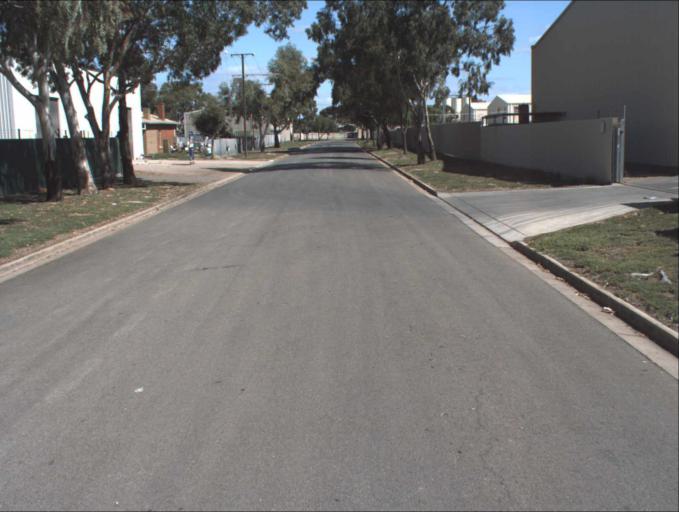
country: AU
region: South Australia
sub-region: Charles Sturt
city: Woodville North
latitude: -34.8374
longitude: 138.5516
